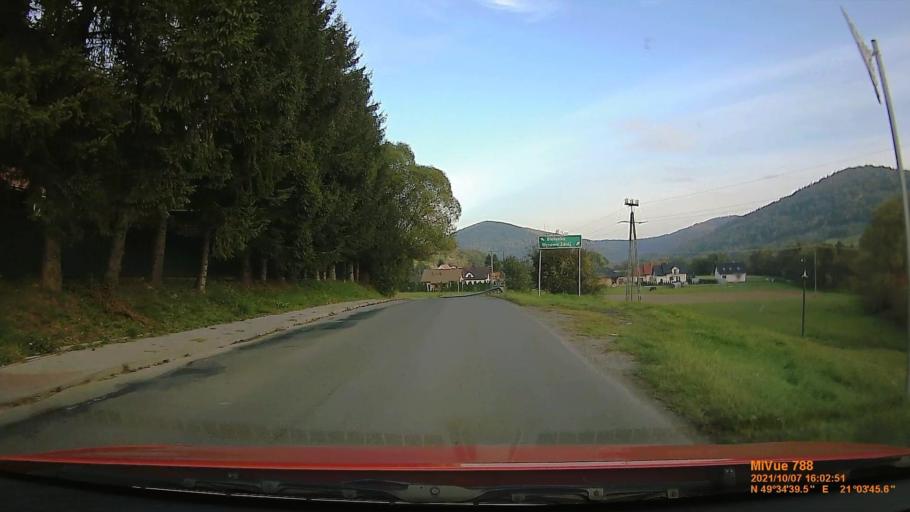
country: PL
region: Lesser Poland Voivodeship
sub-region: Powiat gorlicki
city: Ropa
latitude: 49.5776
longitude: 21.0628
